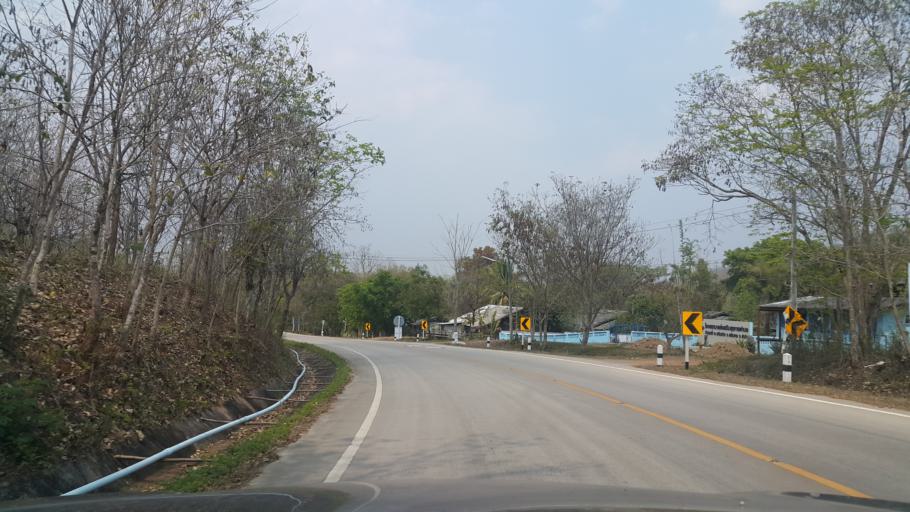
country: TH
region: Lamphun
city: Thung Hua Chang
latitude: 17.9331
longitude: 99.1518
